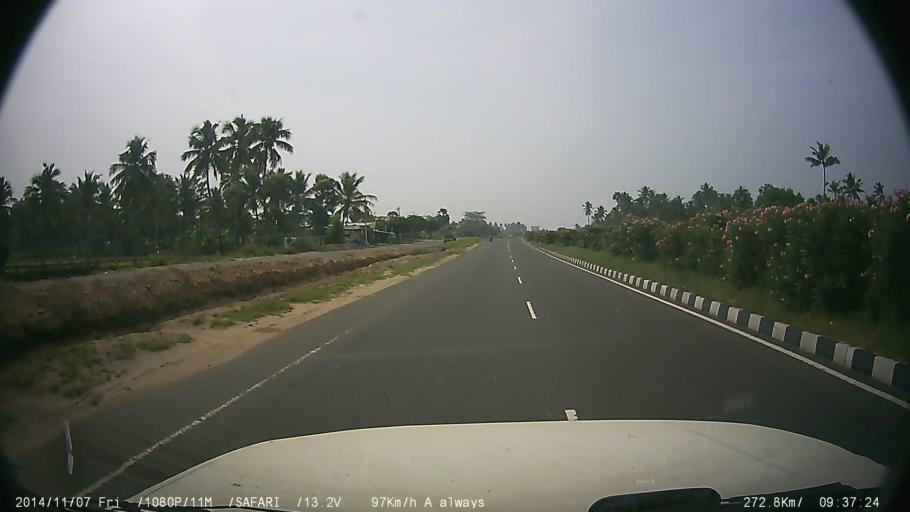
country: IN
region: Tamil Nadu
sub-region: Erode
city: Erode
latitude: 11.3549
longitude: 77.6448
